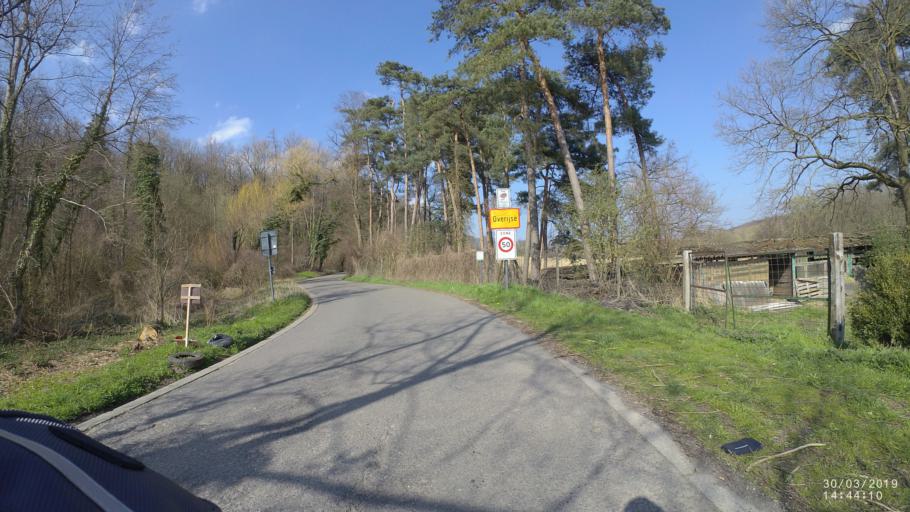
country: BE
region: Flanders
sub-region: Provincie Vlaams-Brabant
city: Overijse
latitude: 50.7447
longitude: 4.5592
